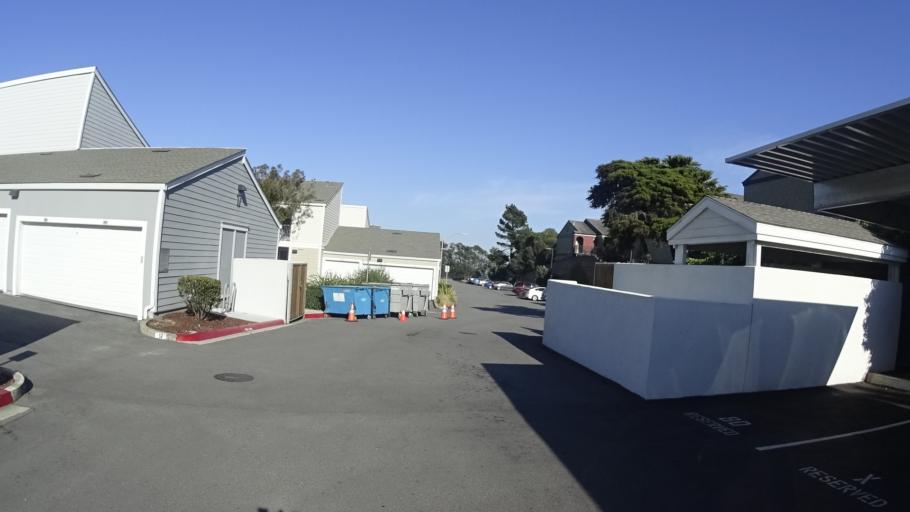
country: US
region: California
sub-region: San Mateo County
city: Pacifica
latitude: 37.6367
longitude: -122.4645
